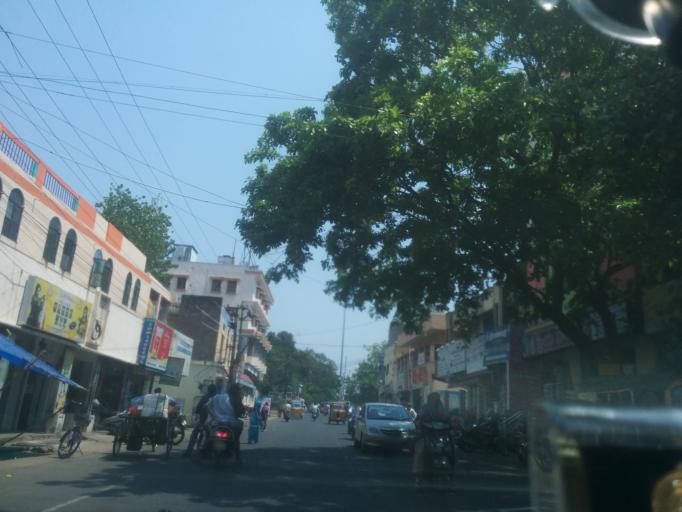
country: IN
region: Andhra Pradesh
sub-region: East Godavari
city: Rajahmundry
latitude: 17.0208
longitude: 81.7744
